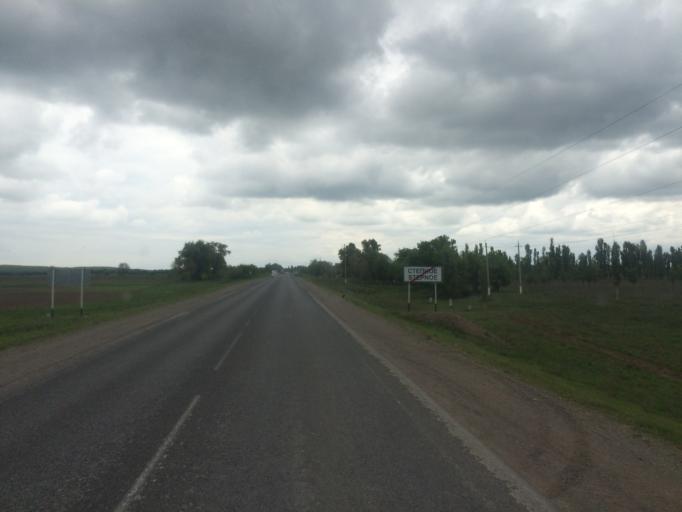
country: KZ
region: Zhambyl
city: Georgiyevka
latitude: 43.1368
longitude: 74.6231
